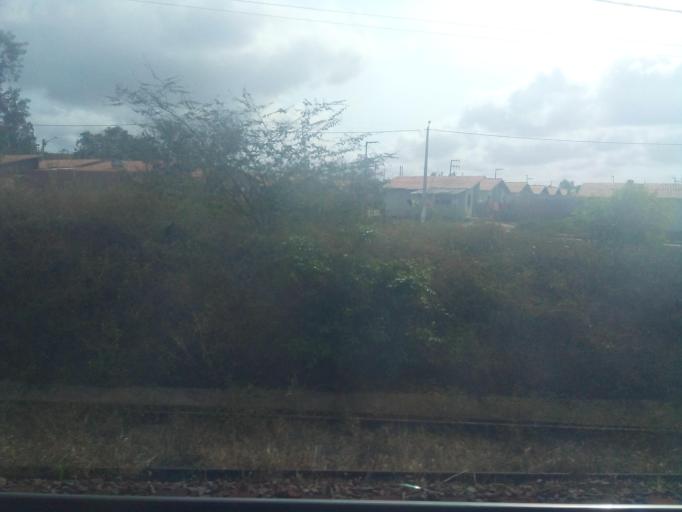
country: BR
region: Maranhao
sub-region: Sao Luis
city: Sao Luis
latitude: -2.6484
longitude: -44.3038
